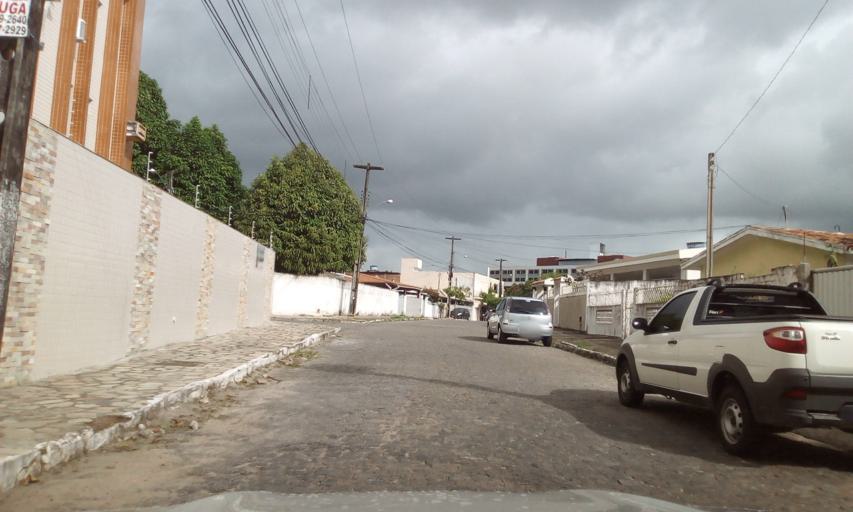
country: BR
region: Paraiba
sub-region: Joao Pessoa
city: Joao Pessoa
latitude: -7.1270
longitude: -34.8577
